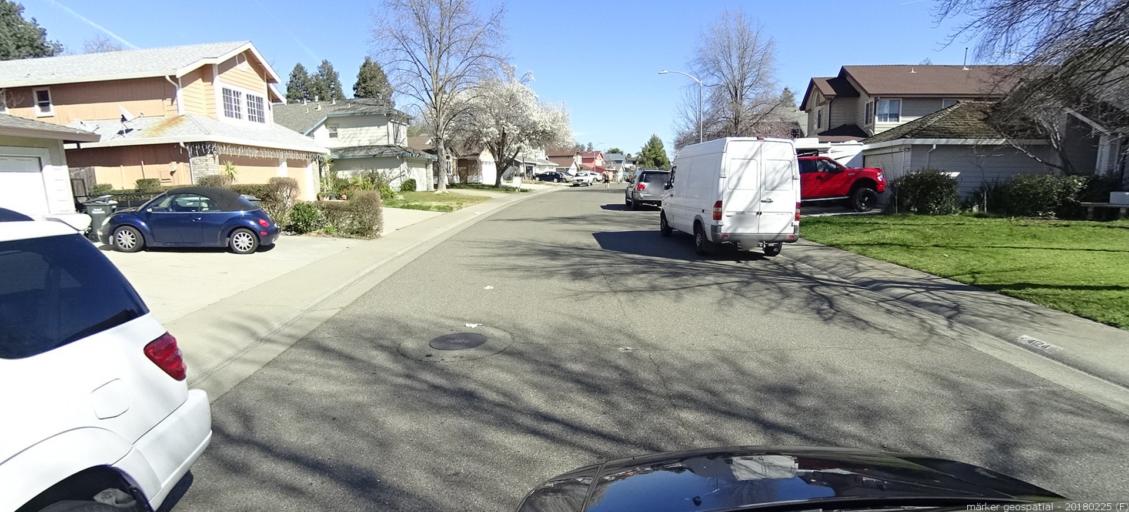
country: US
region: California
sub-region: Sacramento County
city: North Highlands
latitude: 38.7251
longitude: -121.3679
